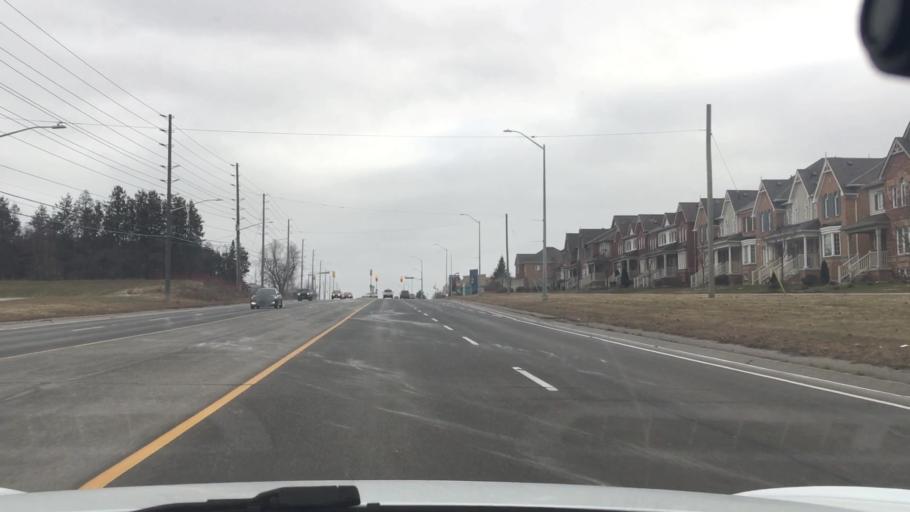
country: CA
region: Ontario
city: Ajax
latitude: 43.8965
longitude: -79.0369
